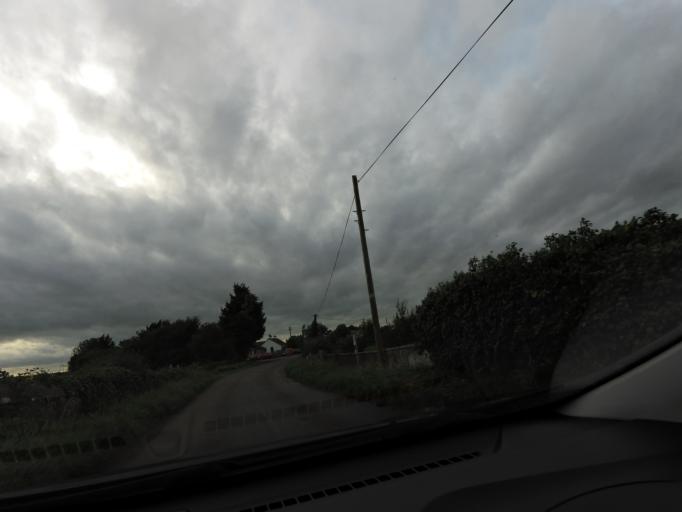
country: IE
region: Leinster
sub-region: Uibh Fhaili
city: Ferbane
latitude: 53.2198
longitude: -7.7979
